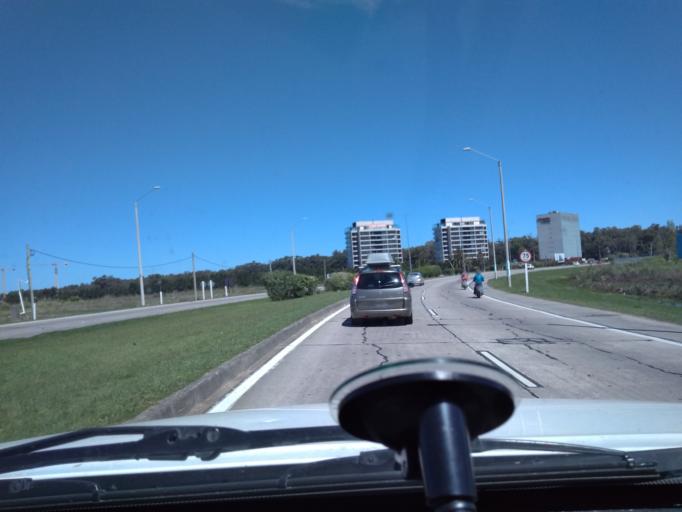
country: UY
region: Canelones
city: Barra de Carrasco
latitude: -34.8473
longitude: -56.0237
